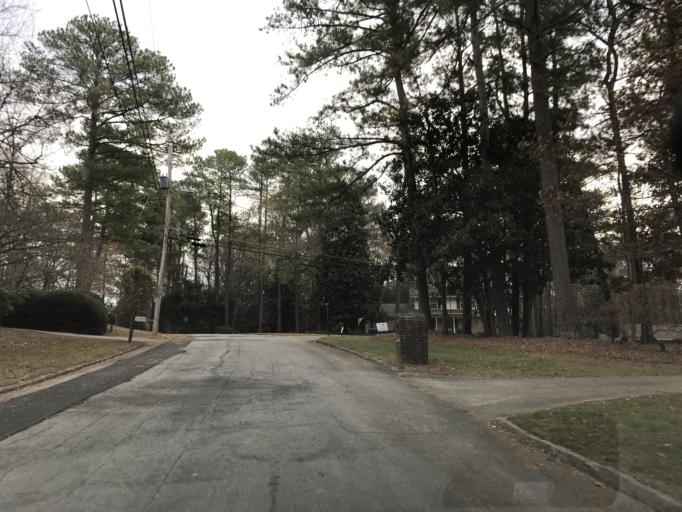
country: US
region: Georgia
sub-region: DeKalb County
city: Doraville
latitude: 33.8818
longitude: -84.2547
